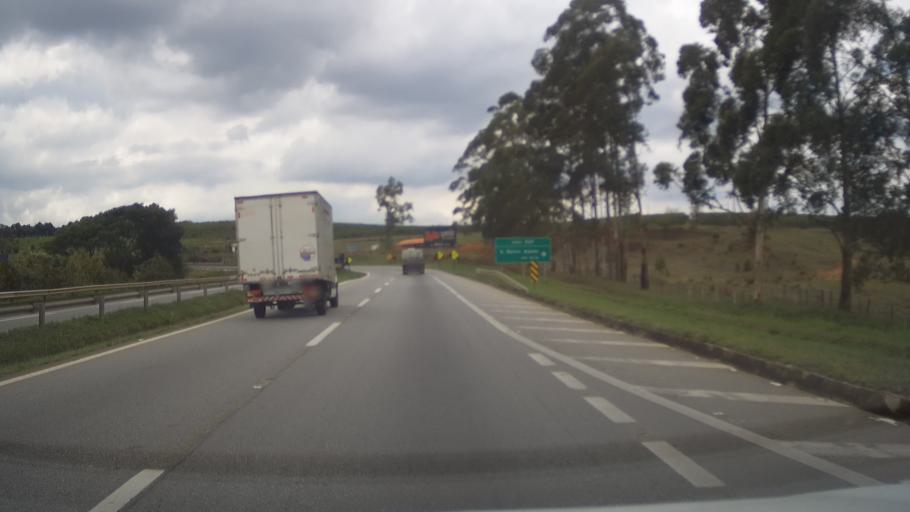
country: BR
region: Minas Gerais
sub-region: Tres Coracoes
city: Tres Coracoes
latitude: -21.4809
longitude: -45.2021
